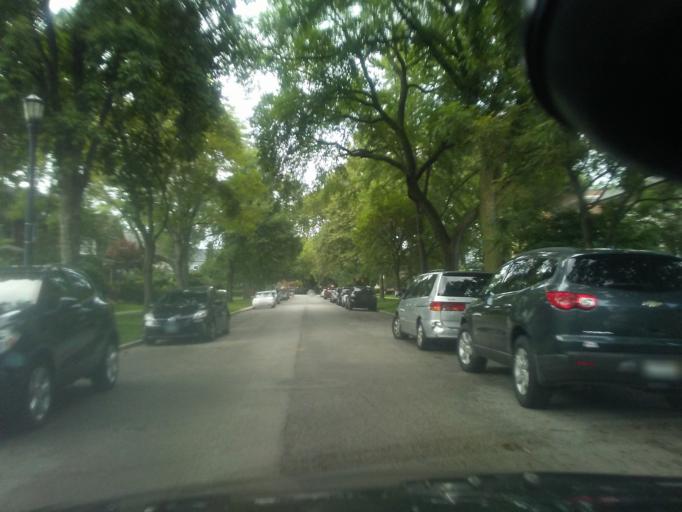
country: US
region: Illinois
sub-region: Cook County
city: Evanston
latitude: 42.0307
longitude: -87.6738
